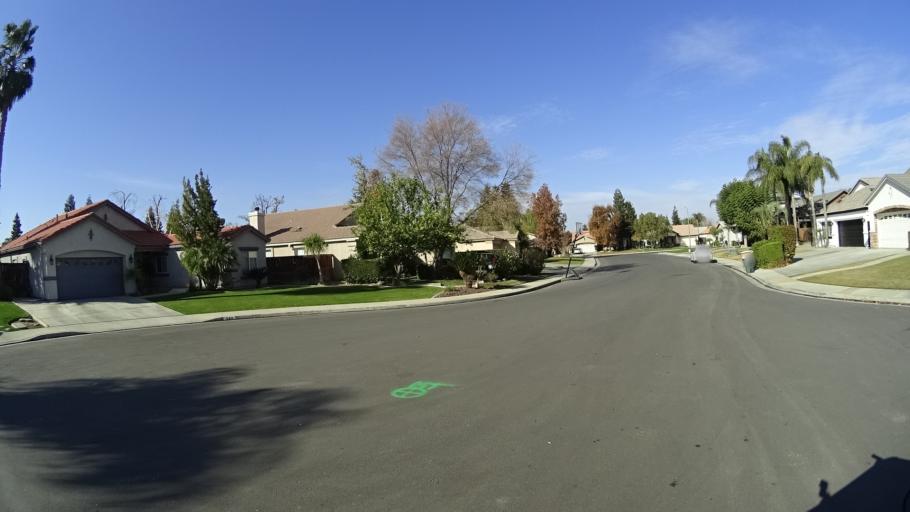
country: US
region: California
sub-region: Kern County
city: Greenacres
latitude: 35.4091
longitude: -119.0963
